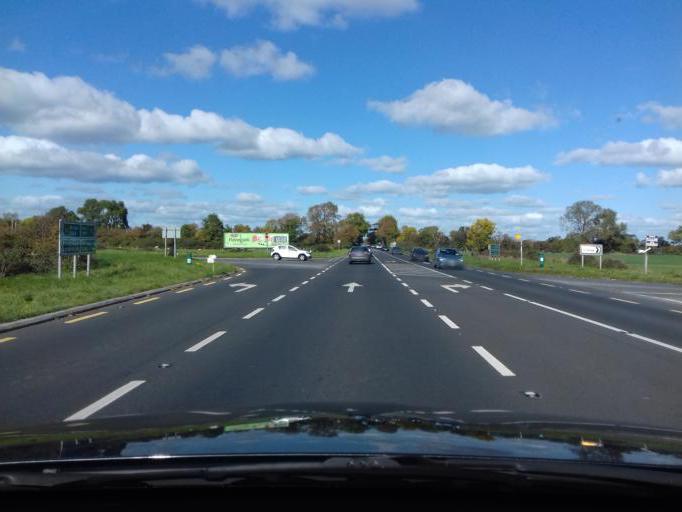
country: IE
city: Kentstown
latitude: 53.6023
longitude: -6.4715
